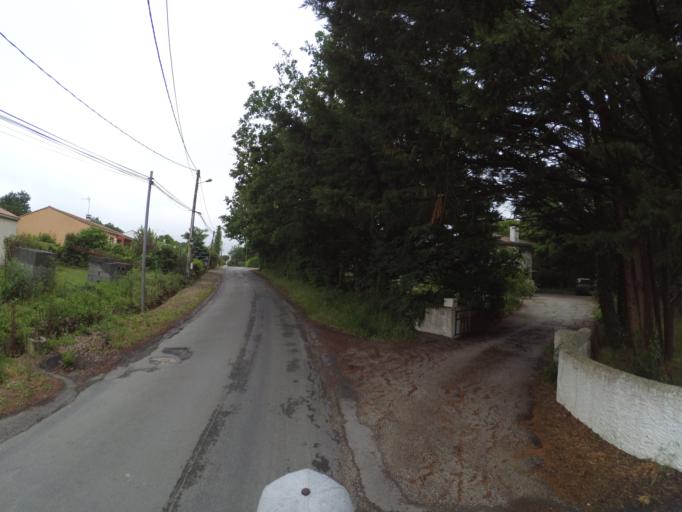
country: FR
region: Pays de la Loire
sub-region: Departement de la Vendee
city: La Roche-sur-Yon
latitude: 46.6371
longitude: -1.4317
